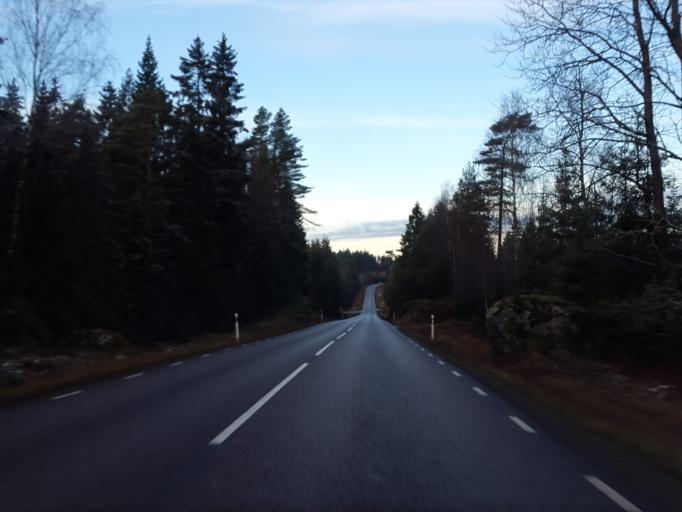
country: SE
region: Vaestra Goetaland
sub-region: Boras Kommun
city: Sandared
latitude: 57.7735
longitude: 12.8042
